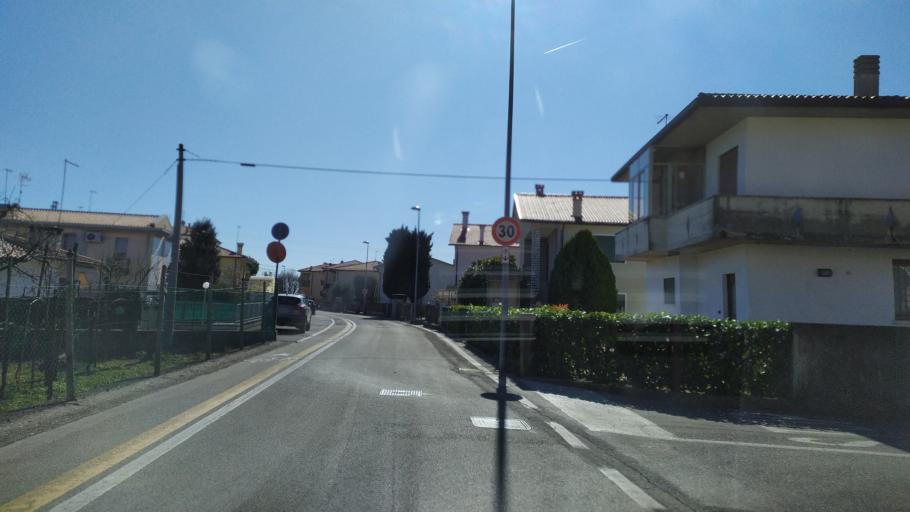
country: IT
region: Veneto
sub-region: Provincia di Vicenza
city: Breganze
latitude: 45.7047
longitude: 11.5680
